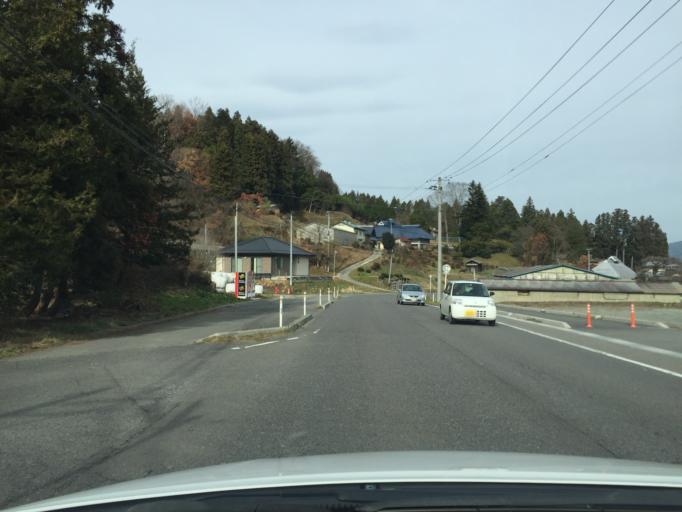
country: JP
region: Fukushima
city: Funehikimachi-funehiki
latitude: 37.4193
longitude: 140.5831
